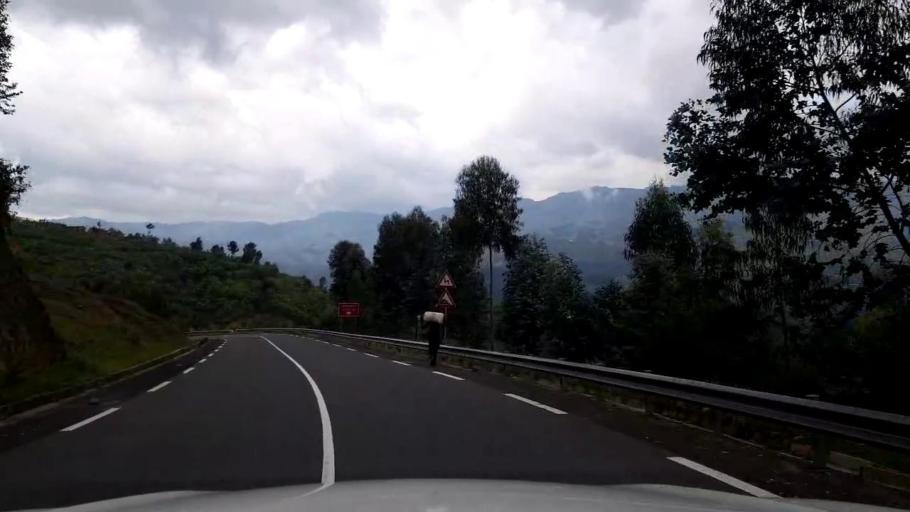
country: RW
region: Western Province
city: Kibuye
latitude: -1.9045
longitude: 29.3590
